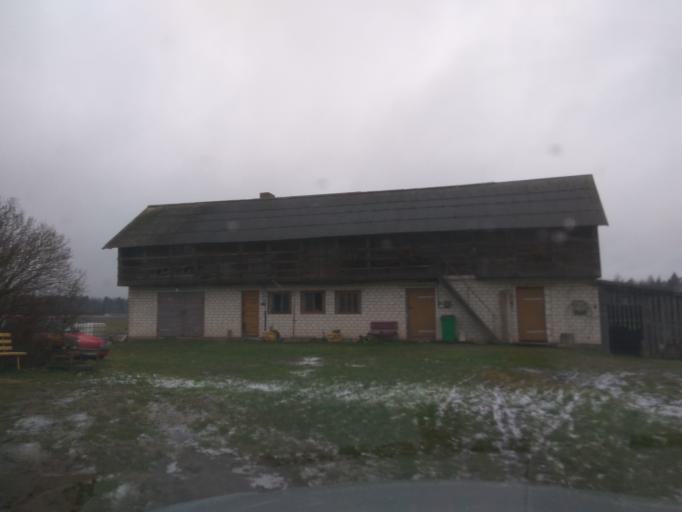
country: LV
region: Saldus Rajons
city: Saldus
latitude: 56.8439
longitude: 22.3785
